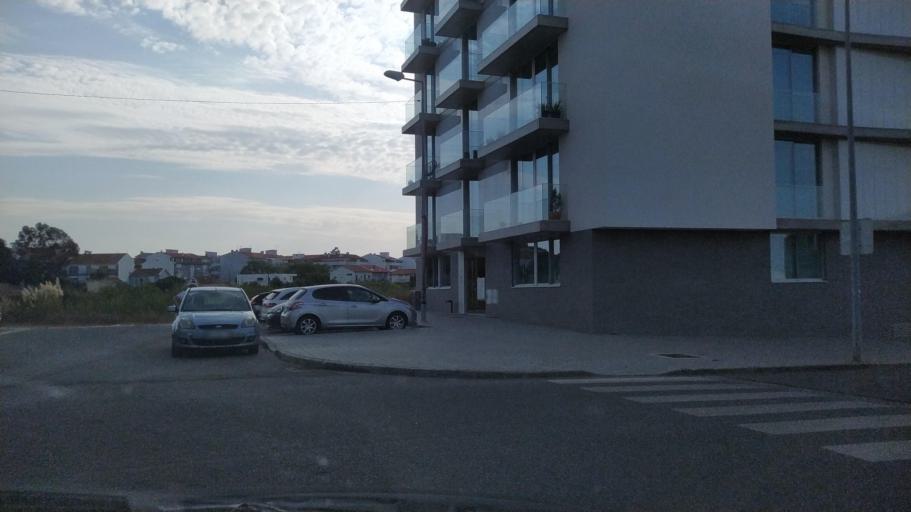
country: PT
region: Aveiro
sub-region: Aveiro
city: Aveiro
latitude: 40.6474
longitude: -8.6480
